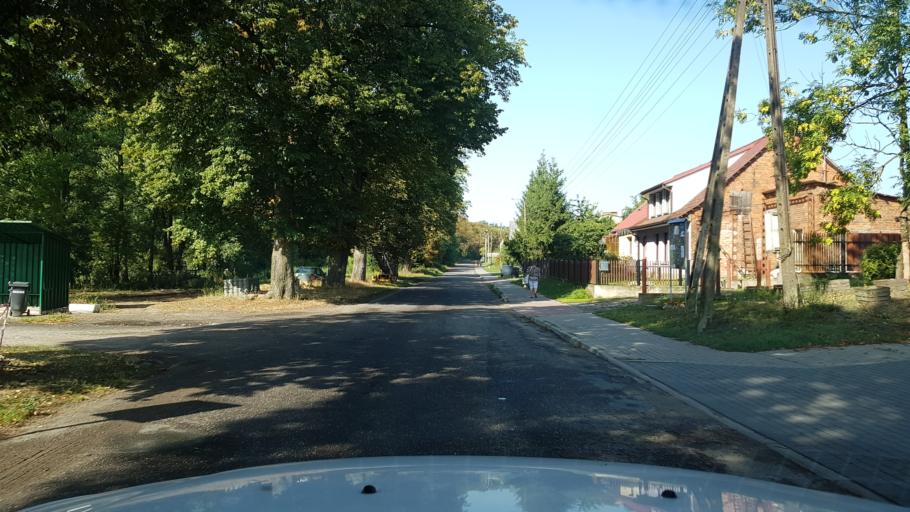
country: PL
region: West Pomeranian Voivodeship
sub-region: Powiat stargardzki
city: Dolice
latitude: 53.2370
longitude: 15.2293
